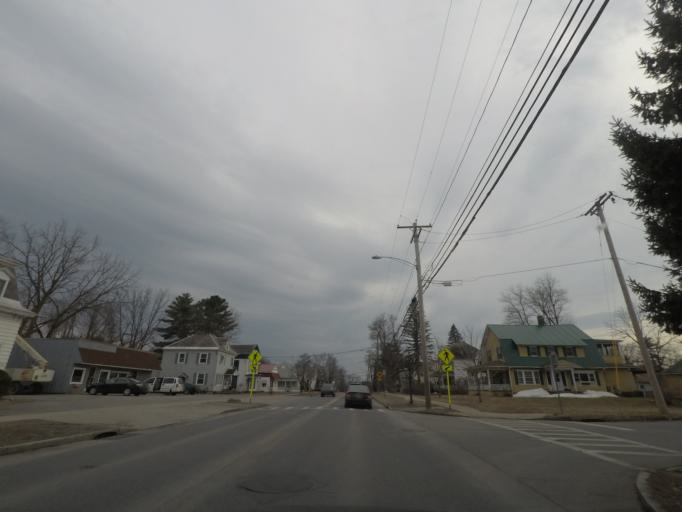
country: US
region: New York
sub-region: Washington County
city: Fort Edward
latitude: 43.2776
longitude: -73.5864
